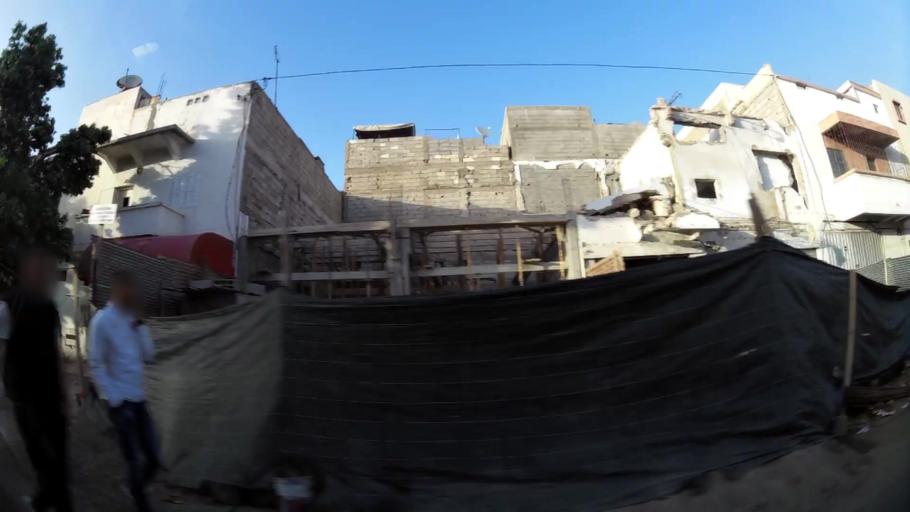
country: MA
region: Oued ed Dahab-Lagouira
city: Dakhla
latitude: 30.4179
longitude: -9.5717
